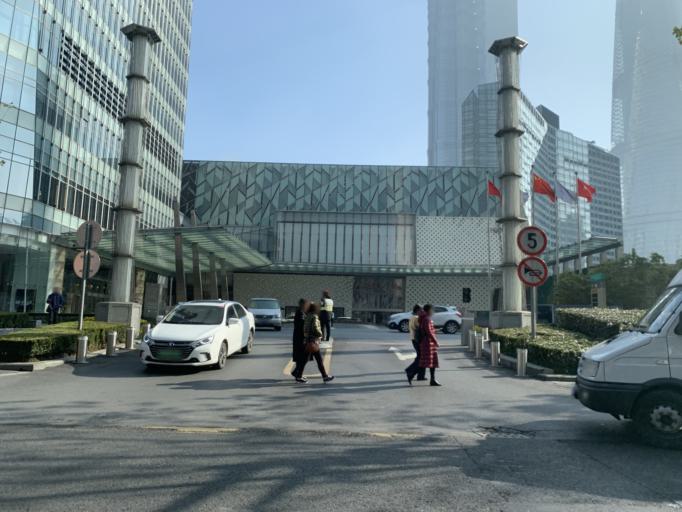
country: CN
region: Shanghai Shi
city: Hongkou
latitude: 31.2381
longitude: 121.4963
